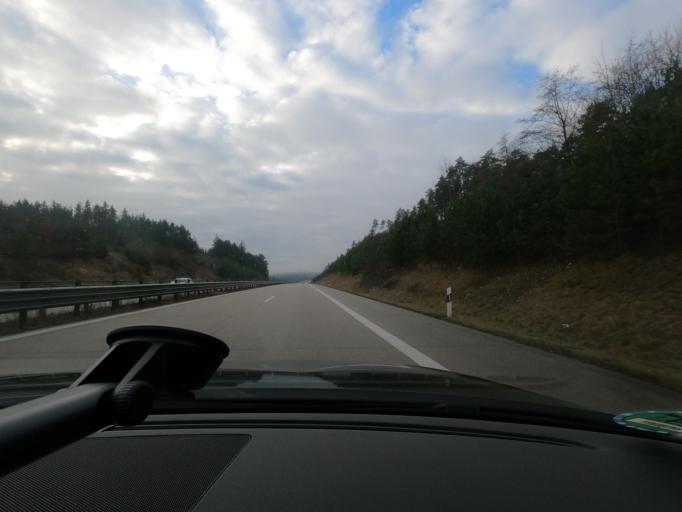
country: DE
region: Bavaria
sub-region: Upper Franconia
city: Niederfullbach
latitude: 50.2138
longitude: 11.0471
